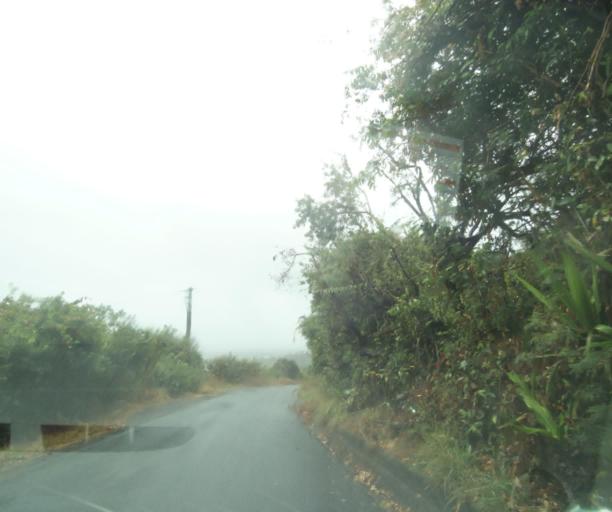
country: RE
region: Reunion
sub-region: Reunion
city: La Possession
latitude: -20.9795
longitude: 55.3350
